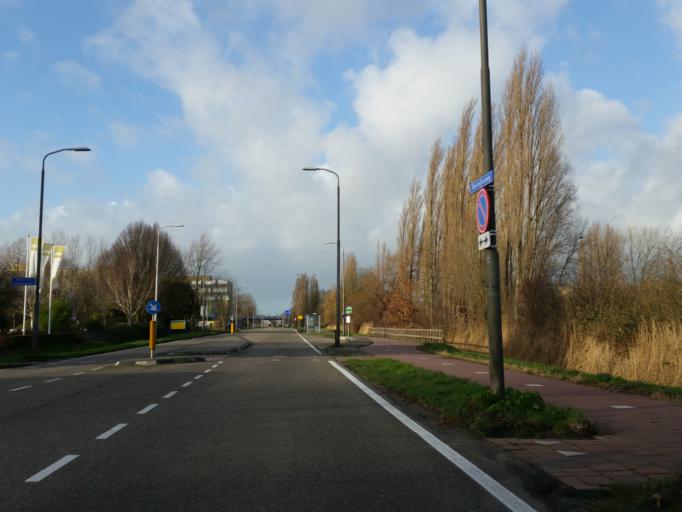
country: NL
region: South Holland
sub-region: Gemeente Zoetermeer
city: Zoetermeer
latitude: 52.0454
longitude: 4.5185
